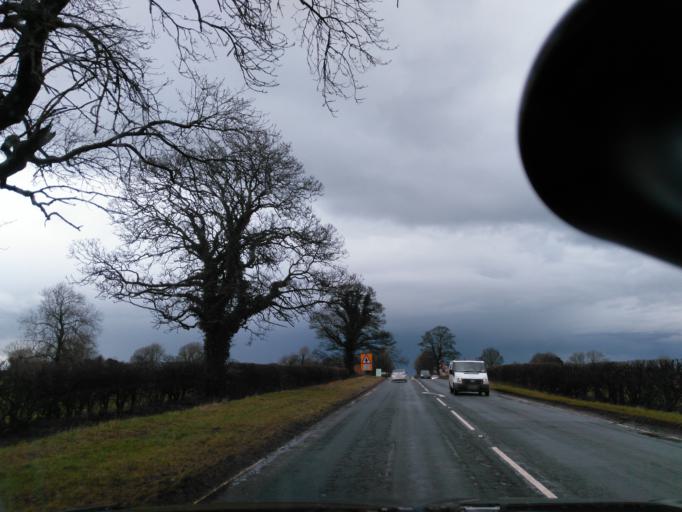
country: GB
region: England
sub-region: North Yorkshire
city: Ripon
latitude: 54.0883
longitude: -1.5301
